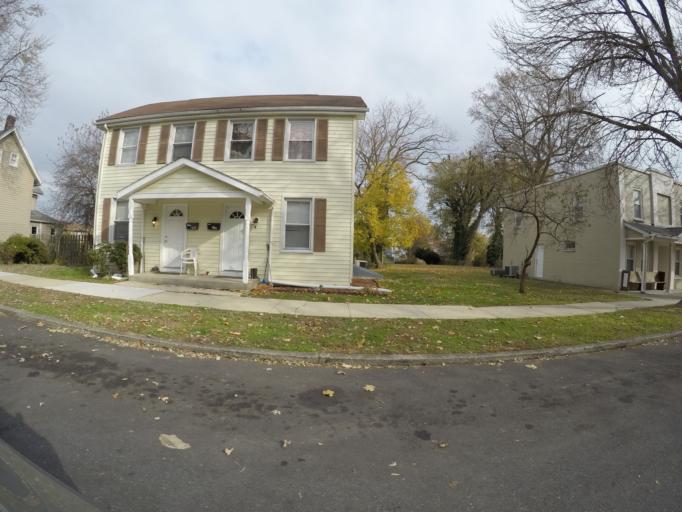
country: US
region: Maryland
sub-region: Harford County
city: Havre de Grace
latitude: 39.5441
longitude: -76.0897
